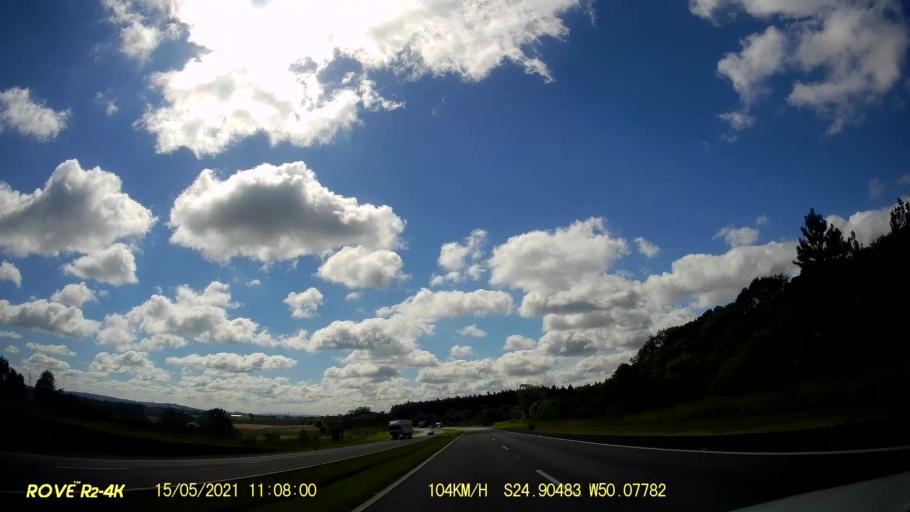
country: BR
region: Parana
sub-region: Carambei
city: Carambei
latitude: -24.9051
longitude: -50.0781
